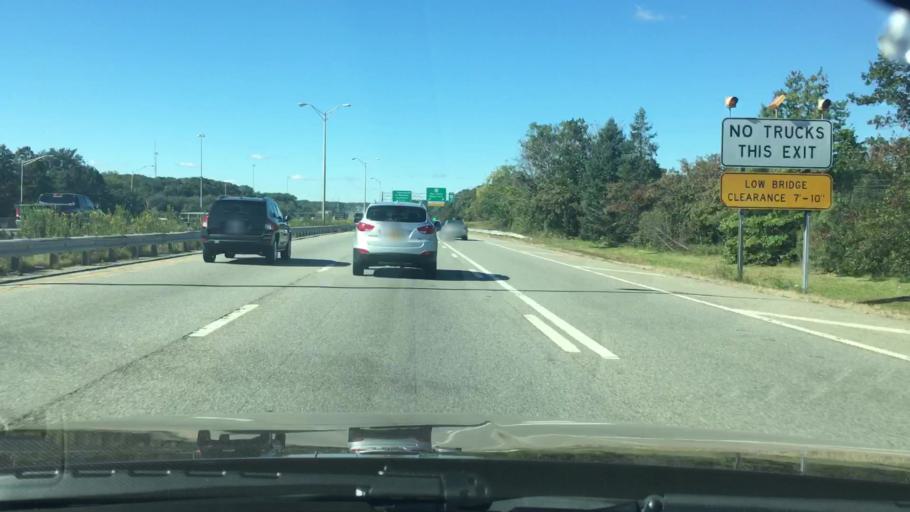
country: US
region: New York
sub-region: Suffolk County
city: Brentwood
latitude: 40.8053
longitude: -73.2724
